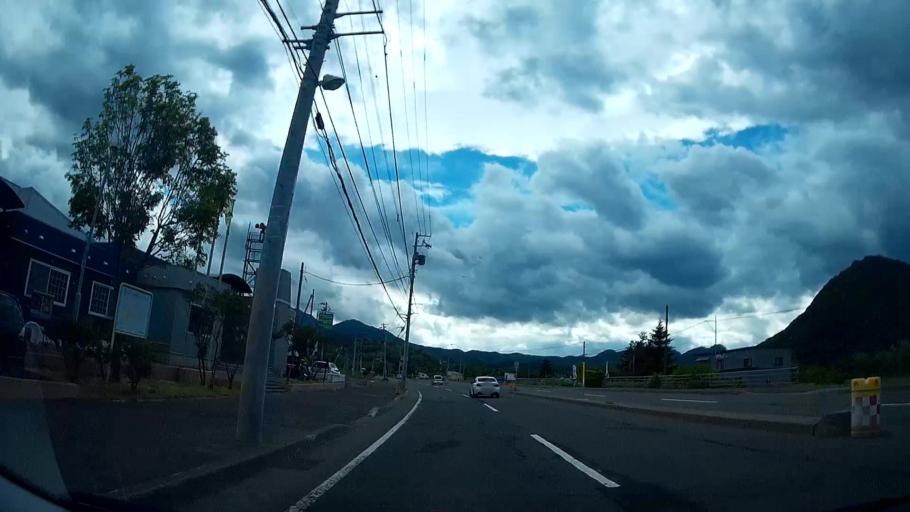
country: JP
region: Hokkaido
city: Sapporo
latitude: 42.9607
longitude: 141.2569
